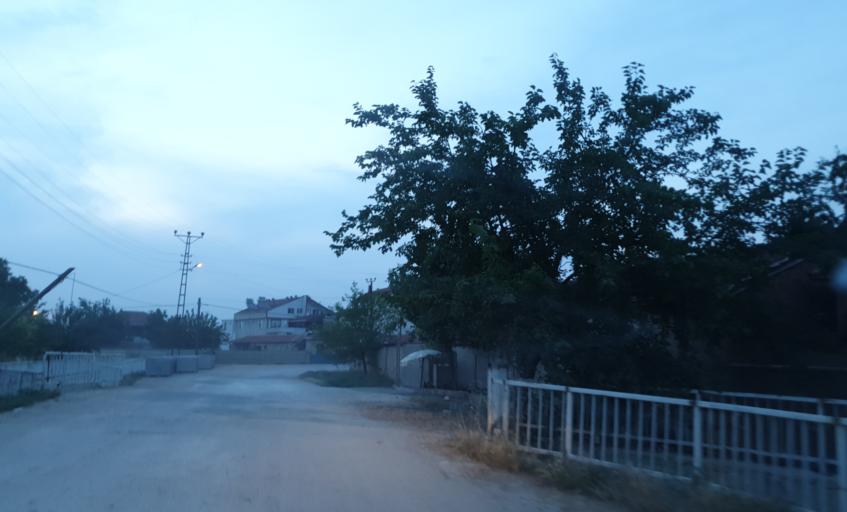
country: TR
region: Kirklareli
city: Vize
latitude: 41.4855
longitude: 27.7532
